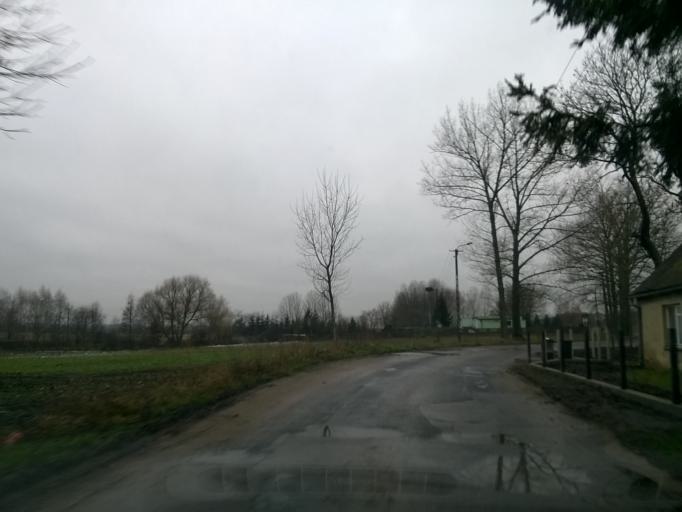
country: PL
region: Kujawsko-Pomorskie
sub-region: Powiat nakielski
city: Naklo nad Notecia
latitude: 53.1330
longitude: 17.5493
